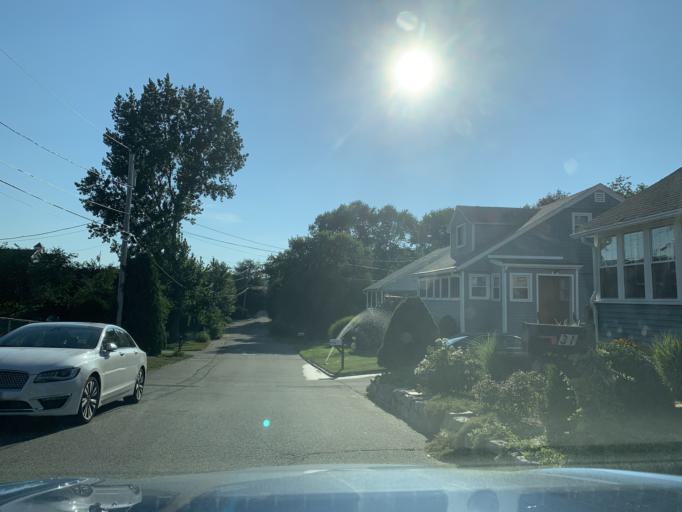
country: US
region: Rhode Island
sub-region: Kent County
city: Warwick
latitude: 41.6877
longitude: -71.4390
